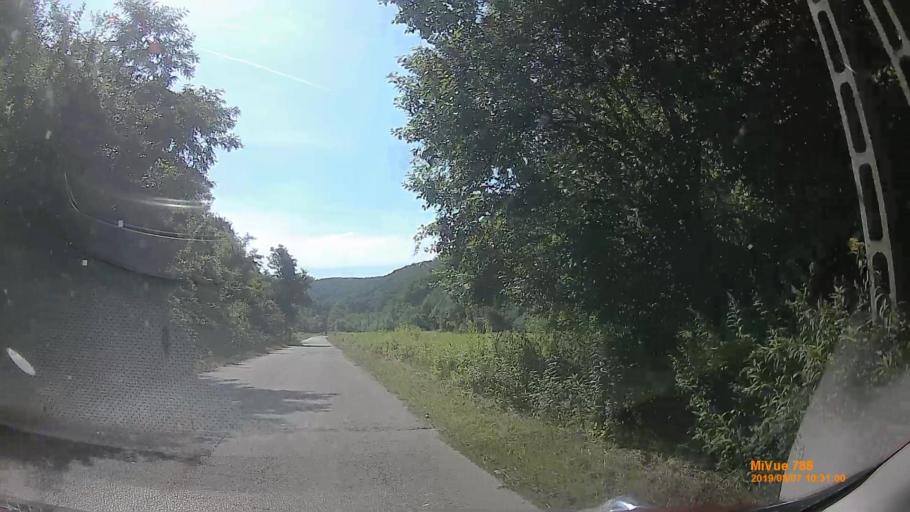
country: HU
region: Veszprem
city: Ajka
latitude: 47.0738
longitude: 17.5814
